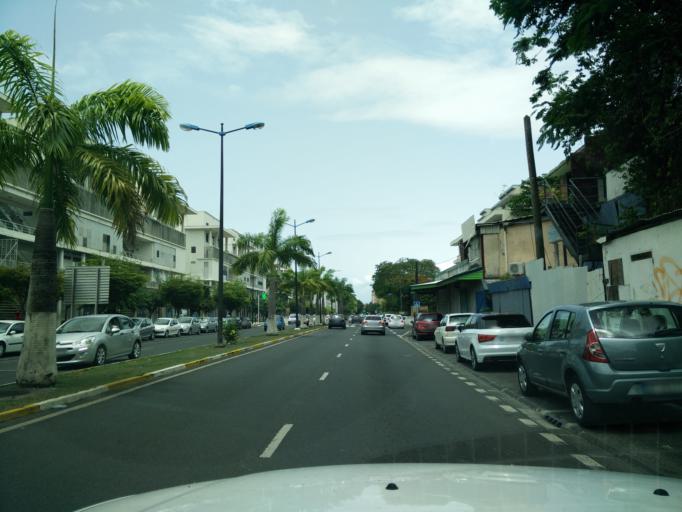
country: GP
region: Guadeloupe
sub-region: Guadeloupe
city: Pointe-a-Pitre
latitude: 16.2461
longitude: -61.5296
